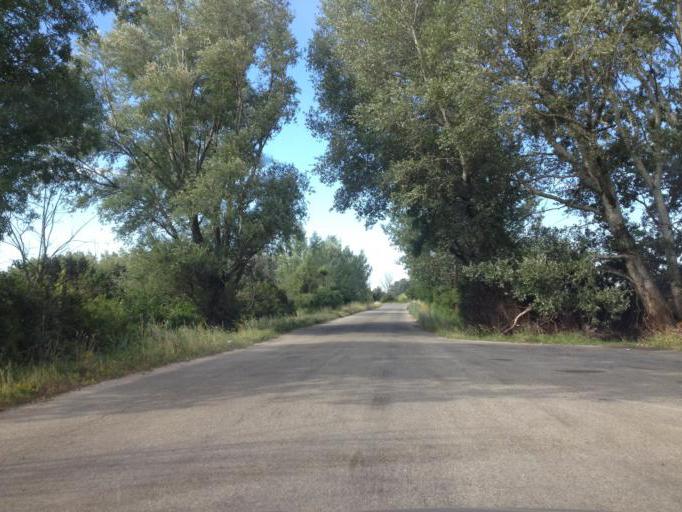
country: FR
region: Provence-Alpes-Cote d'Azur
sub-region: Departement du Vaucluse
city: Orange
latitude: 44.1236
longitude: 4.7957
